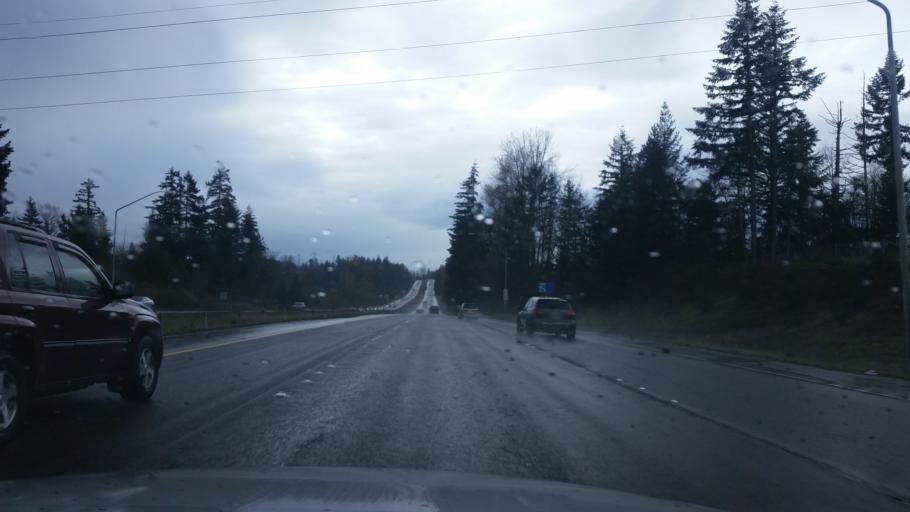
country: US
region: Washington
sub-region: King County
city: Covington
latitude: 47.3547
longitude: -122.1268
